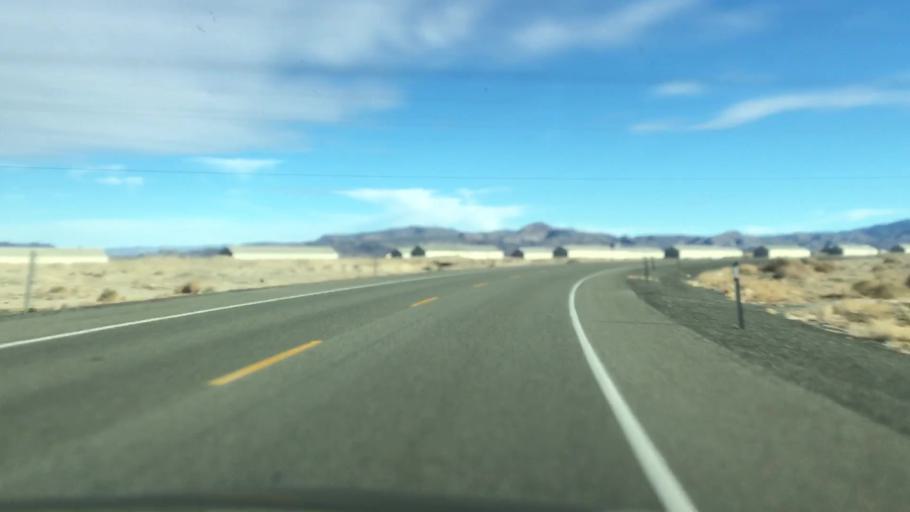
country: US
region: Nevada
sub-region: Mineral County
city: Hawthorne
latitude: 38.5334
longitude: -118.6138
